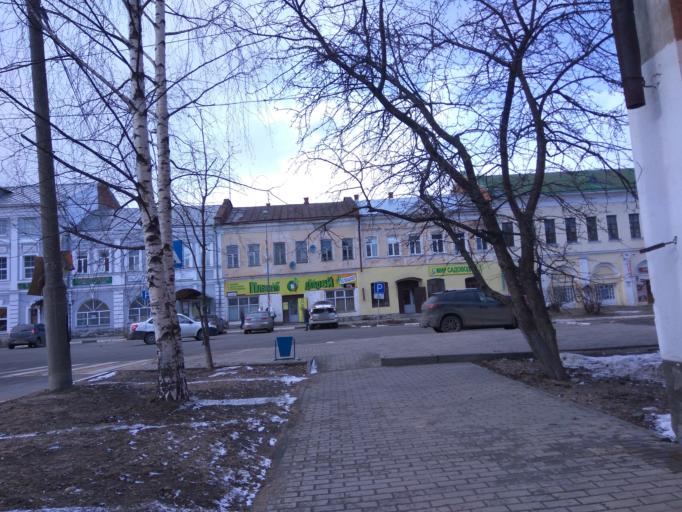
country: RU
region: Jaroslavl
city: Rostov
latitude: 57.1865
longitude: 39.4190
